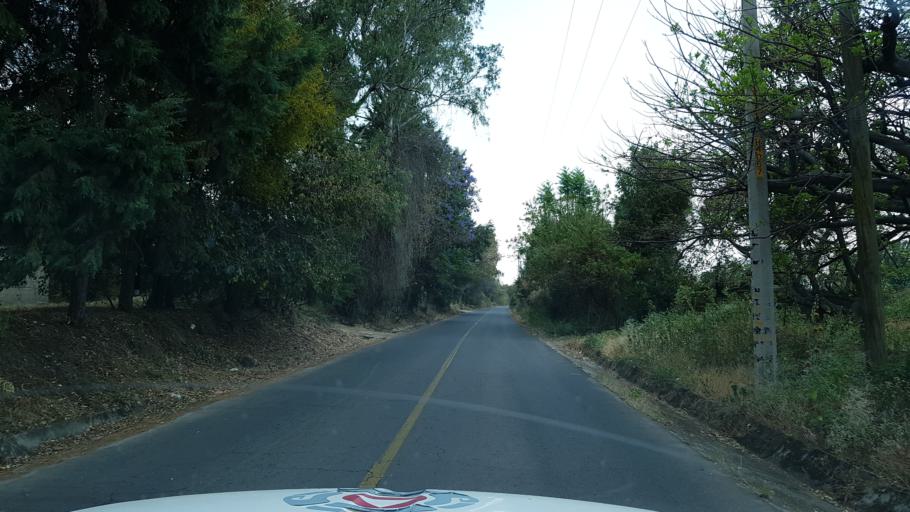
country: MX
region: Morelos
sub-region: Yecapixtla
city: Texcala
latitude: 18.9117
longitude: -98.8077
